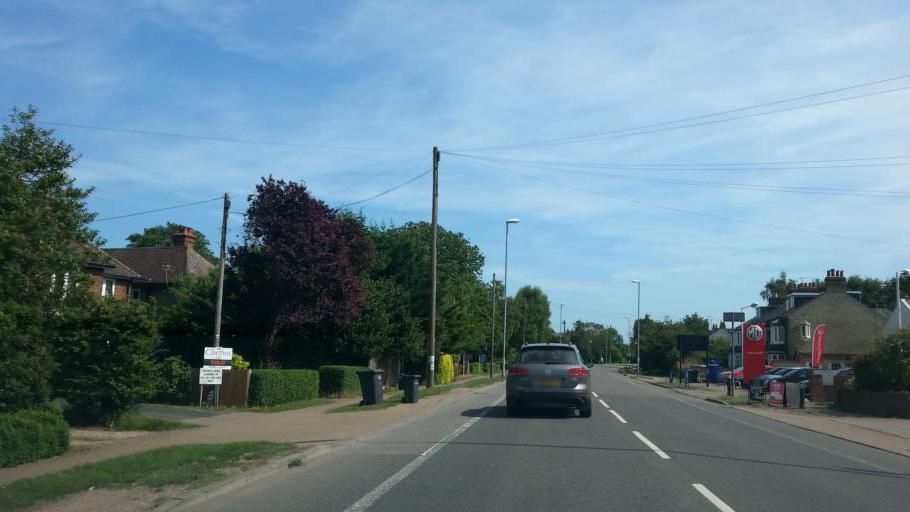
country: GB
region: England
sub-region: Cambridgeshire
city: Grantchester
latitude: 52.1663
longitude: 0.1192
